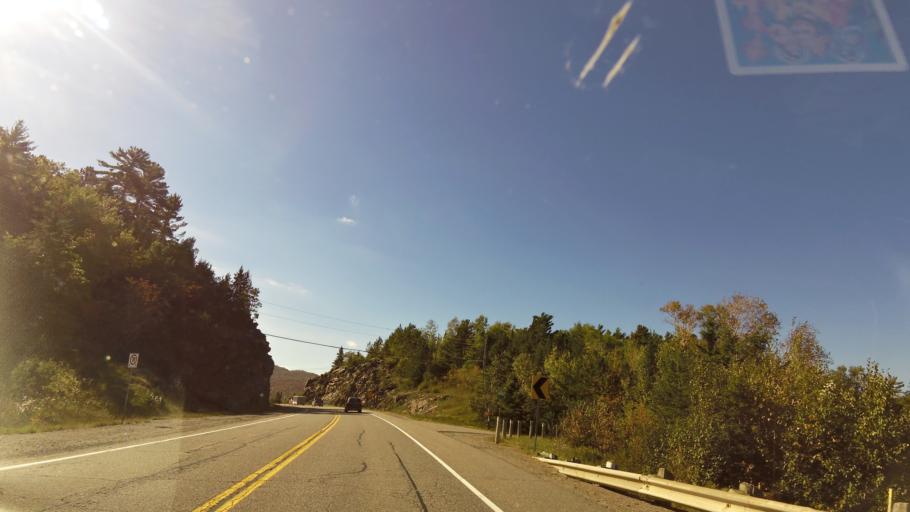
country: CA
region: Ontario
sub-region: Algoma
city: Sault Ste. Marie
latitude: 46.8261
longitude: -84.3987
